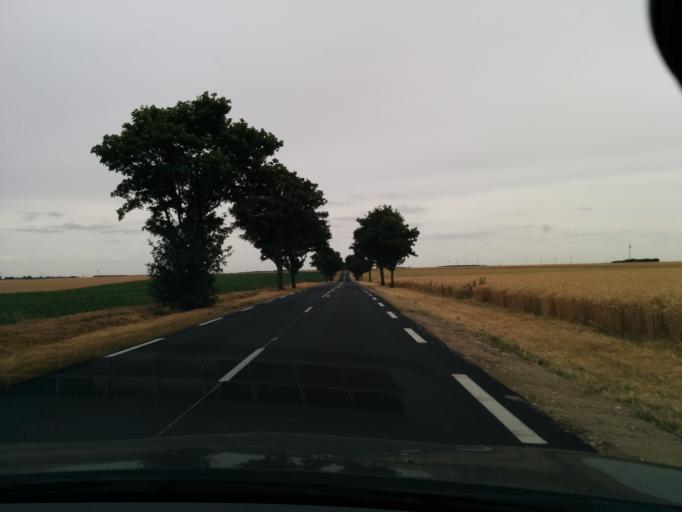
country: FR
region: Ile-de-France
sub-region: Departement de l'Essonne
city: Pussay
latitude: 48.3963
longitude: 1.9720
